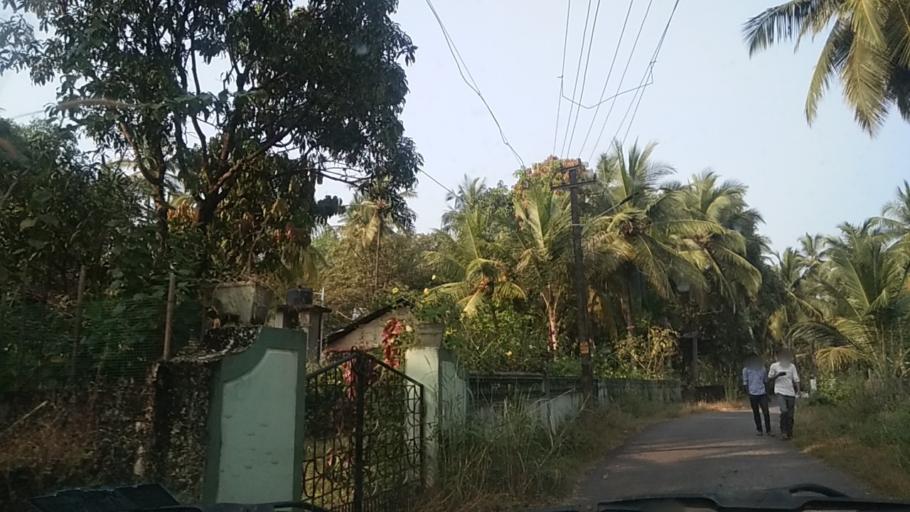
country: IN
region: Goa
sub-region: South Goa
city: Colva
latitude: 15.3092
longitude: 73.9316
